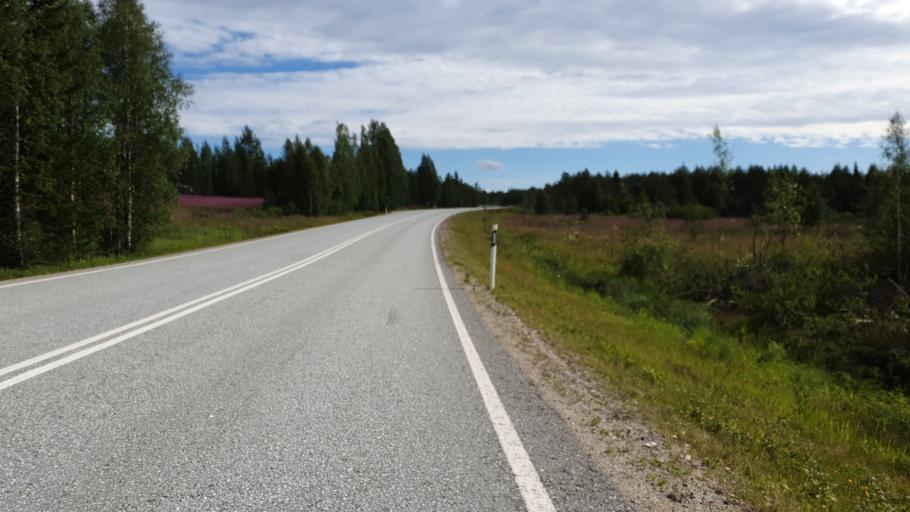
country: FI
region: Kainuu
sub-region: Kehys-Kainuu
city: Kuhmo
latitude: 64.4994
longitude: 29.9157
